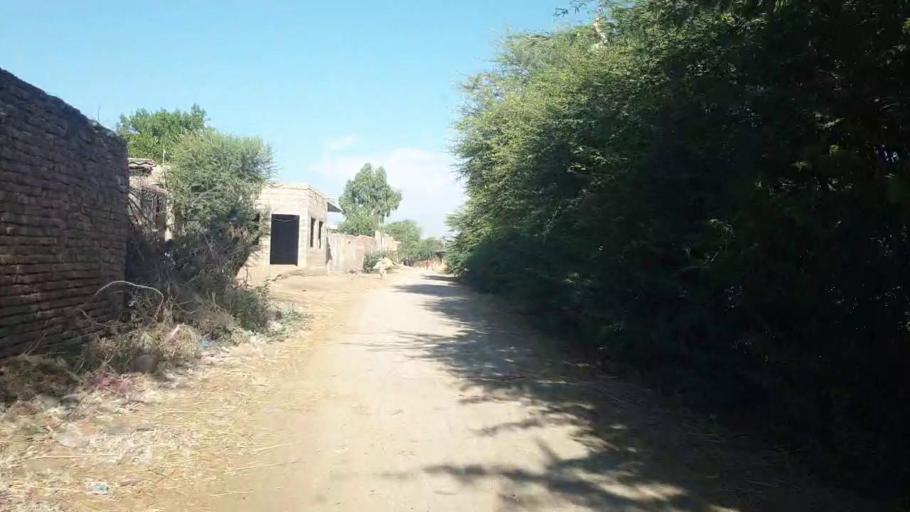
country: PK
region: Sindh
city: Talhar
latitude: 24.8905
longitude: 68.8144
